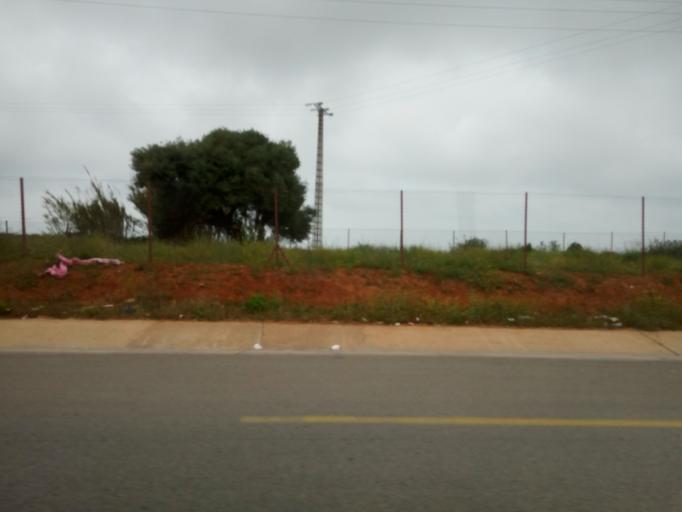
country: DZ
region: Tipaza
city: Bou Ismail
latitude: 36.5964
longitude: 2.6356
